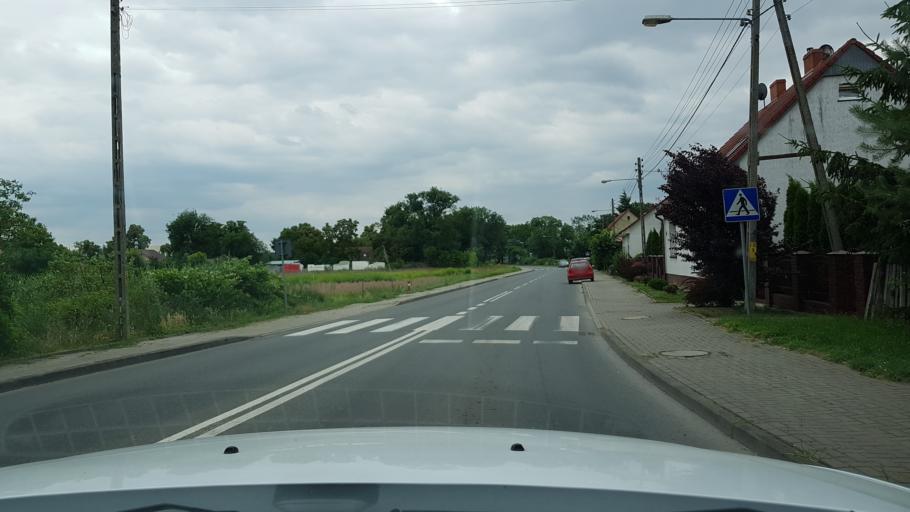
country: PL
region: Lubusz
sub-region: Powiat gorzowski
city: Kostrzyn nad Odra
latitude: 52.6121
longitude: 14.6203
